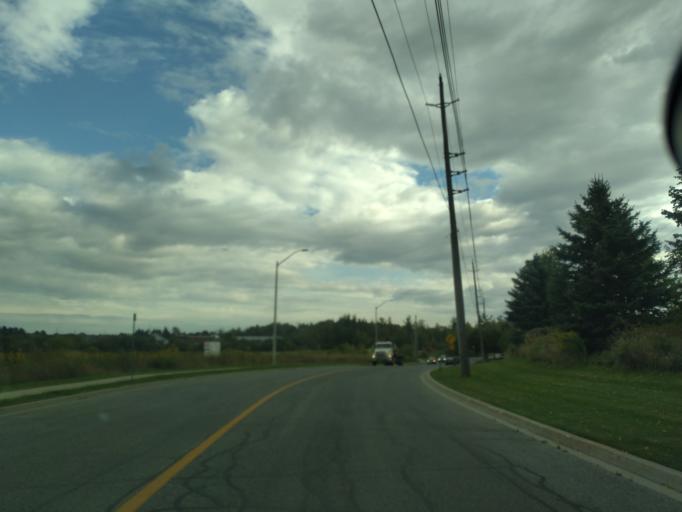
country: CA
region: Ontario
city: Newmarket
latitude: 43.9869
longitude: -79.4596
